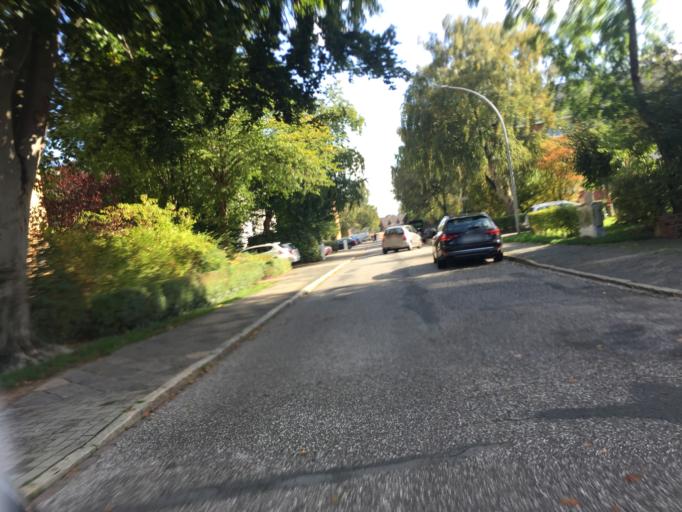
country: DE
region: Schleswig-Holstein
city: Heiligenstedten
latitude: 53.9341
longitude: 9.4930
